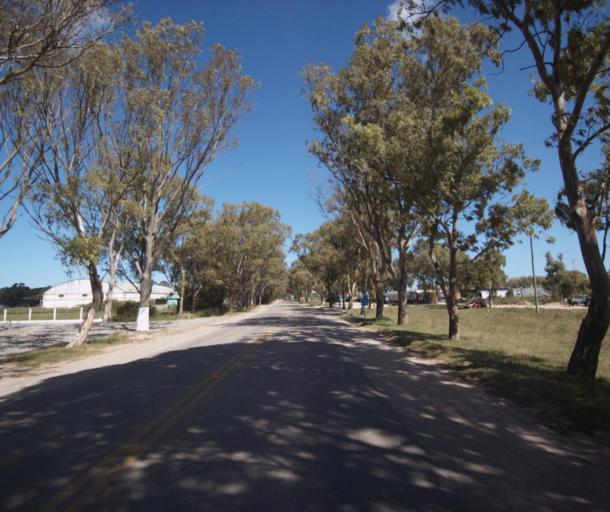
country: BR
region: Rio Grande do Sul
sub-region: Chui
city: Chui
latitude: -33.6850
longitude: -53.4487
